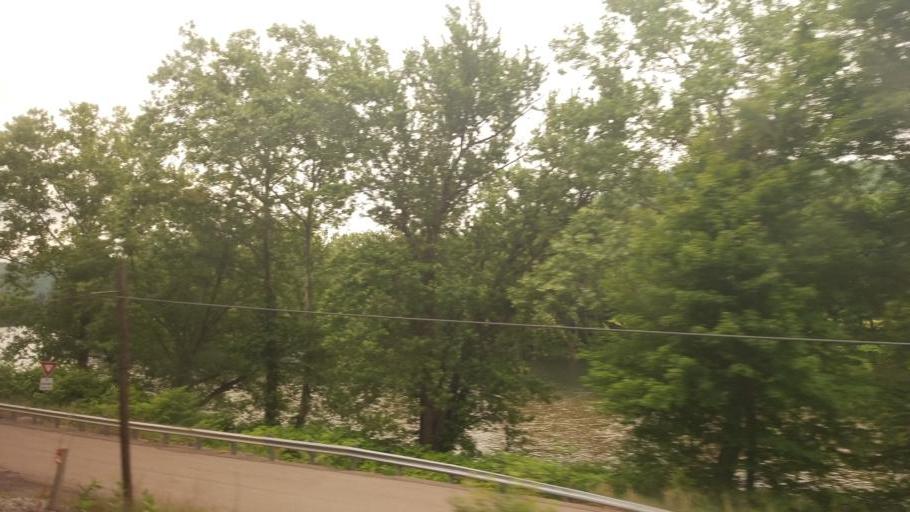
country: US
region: Pennsylvania
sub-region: Fayette County
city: South Connellsville
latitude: 39.8236
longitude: -79.3670
